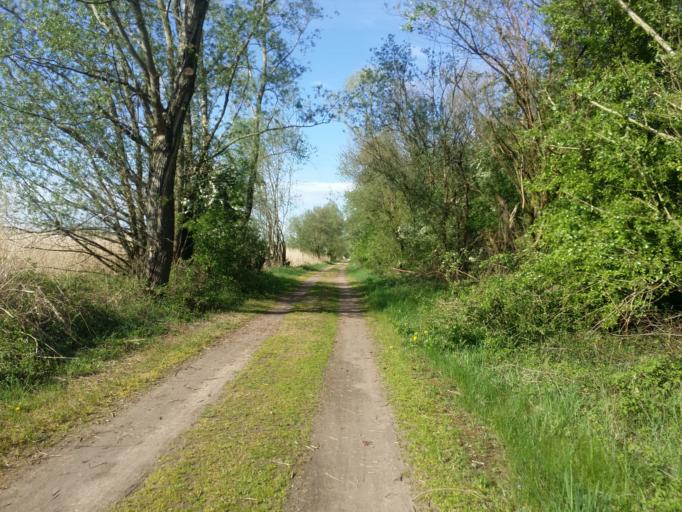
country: DE
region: Lower Saxony
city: Lemwerder
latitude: 53.1435
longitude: 8.6653
